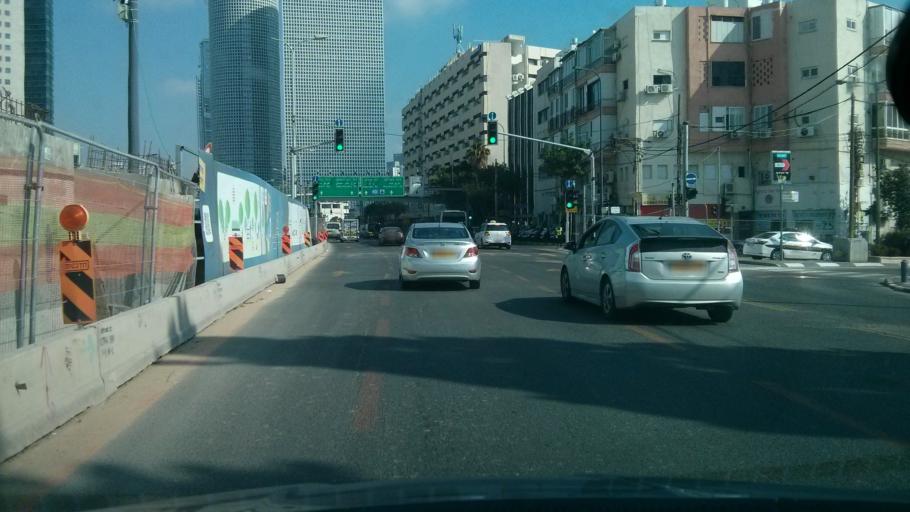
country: IL
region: Tel Aviv
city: Tel Aviv
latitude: 32.0701
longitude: 34.7886
